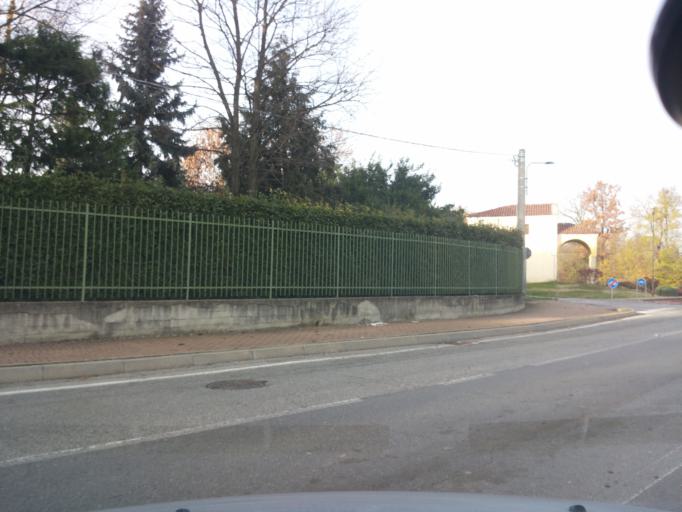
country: IT
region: Piedmont
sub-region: Provincia di Biella
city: Verrone
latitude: 45.5044
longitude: 8.1138
